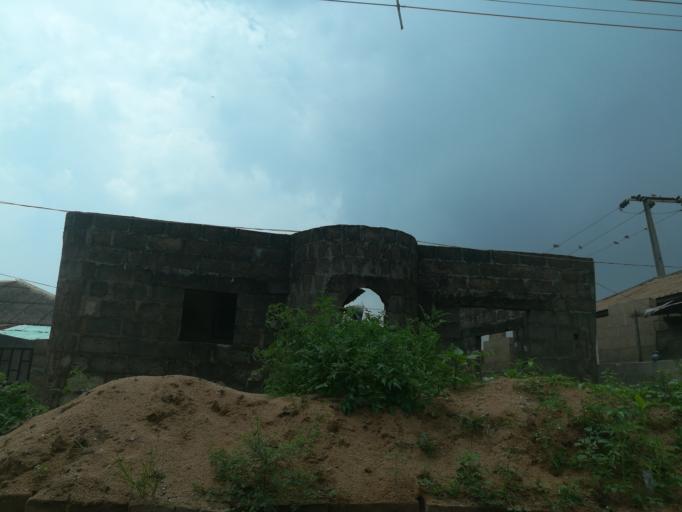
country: NG
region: Lagos
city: Ikorodu
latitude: 6.5697
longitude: 3.5918
